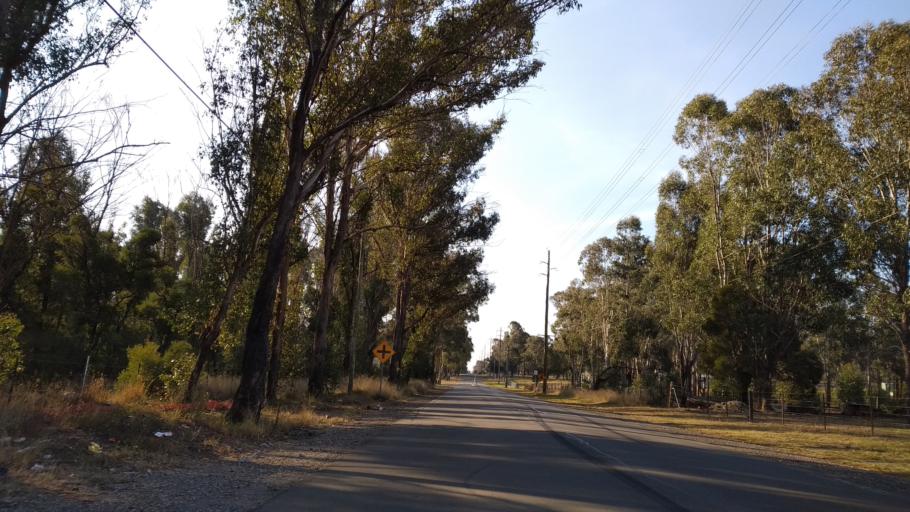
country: AU
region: New South Wales
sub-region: Penrith Municipality
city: Werrington Downs
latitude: -33.7071
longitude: 150.7324
